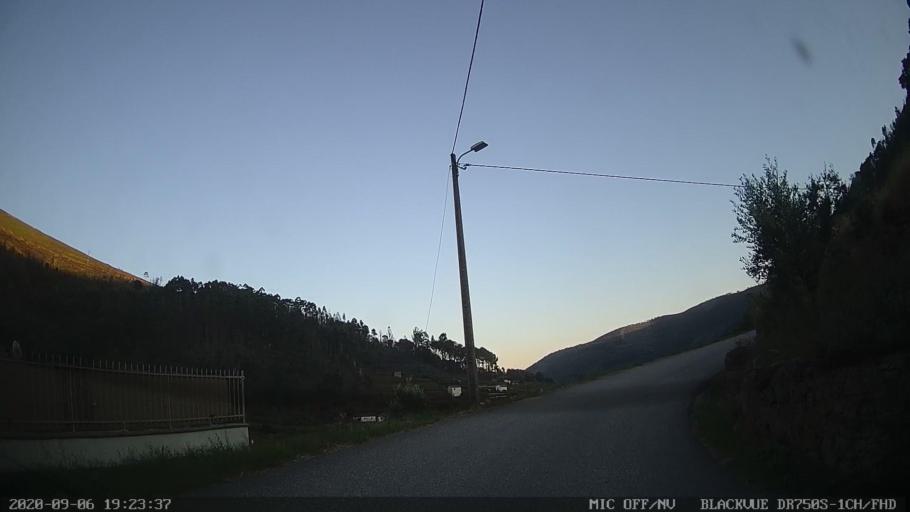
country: PT
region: Vila Real
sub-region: Mesao Frio
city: Mesao Frio
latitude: 41.1893
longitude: -7.9239
